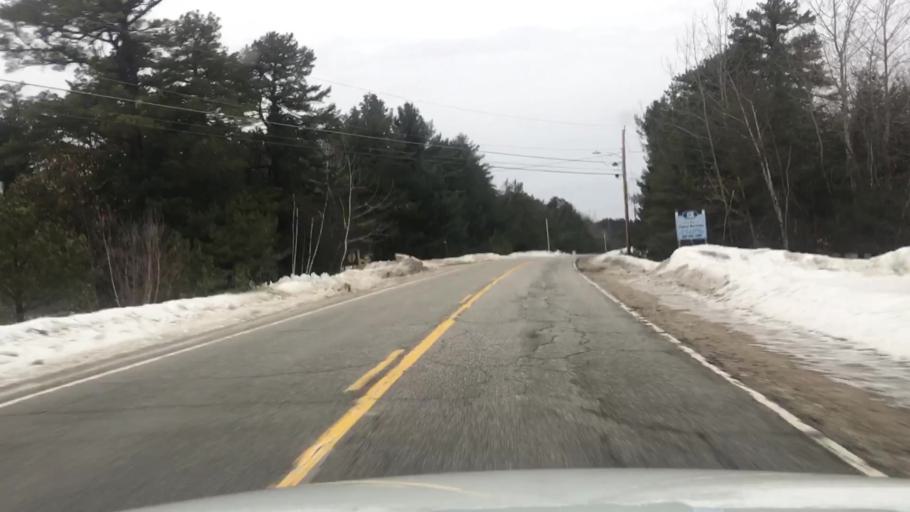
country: US
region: Maine
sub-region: York County
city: Newfield
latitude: 43.5977
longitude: -70.8822
